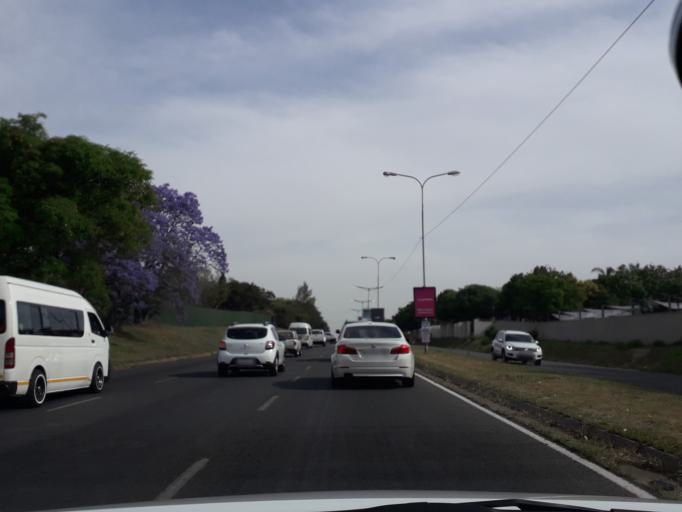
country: ZA
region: Gauteng
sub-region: City of Johannesburg Metropolitan Municipality
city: Johannesburg
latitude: -26.1102
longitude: 28.0310
